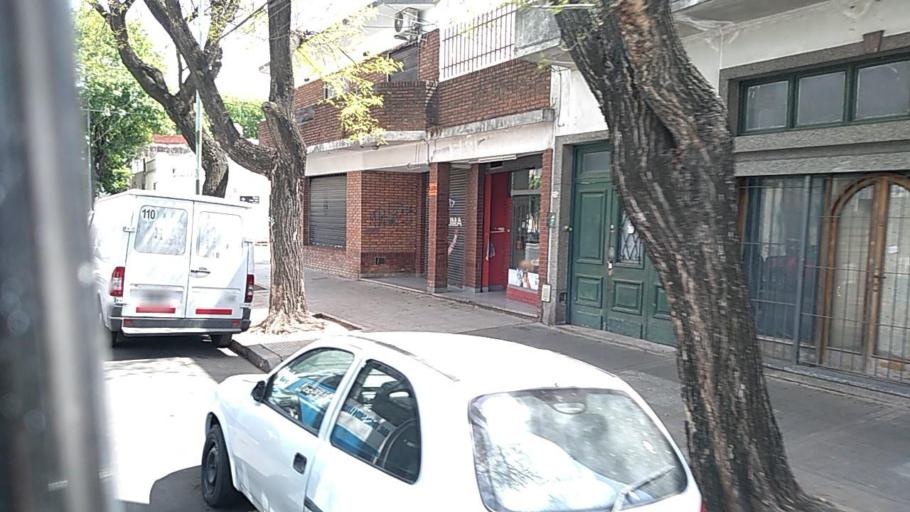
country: AR
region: Buenos Aires F.D.
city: Villa Santa Rita
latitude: -34.6178
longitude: -58.5115
